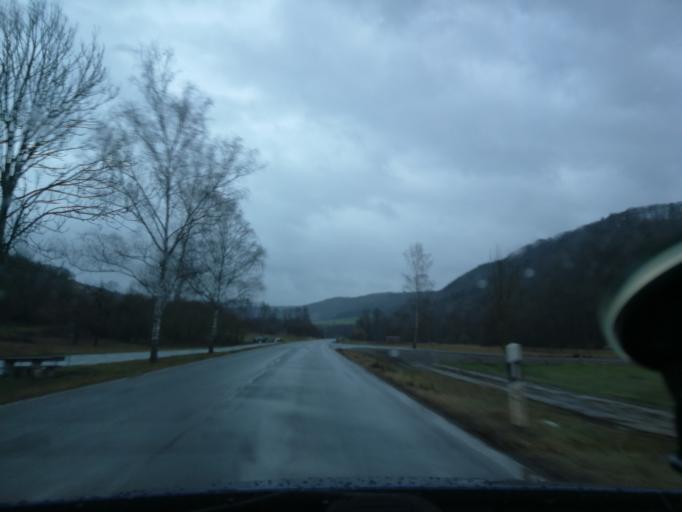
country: DE
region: Rheinland-Pfalz
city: Minheim
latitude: 49.8495
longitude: 6.9261
